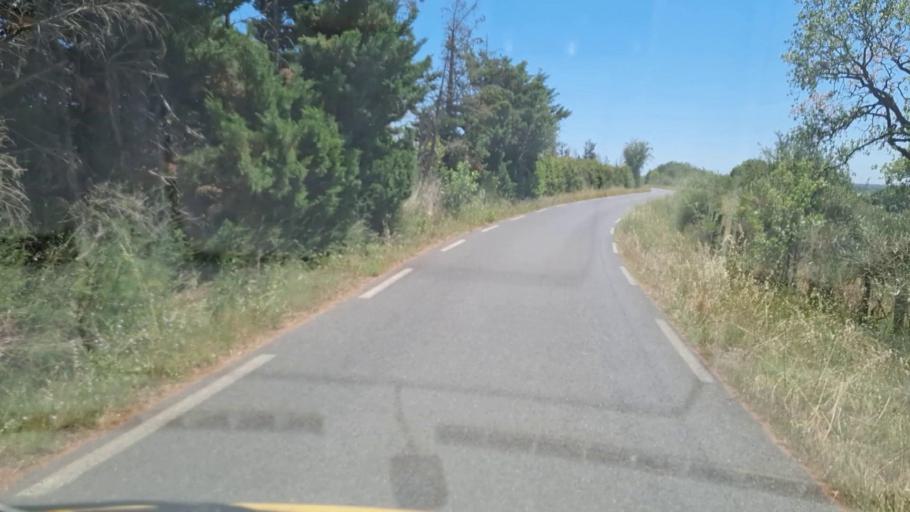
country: FR
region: Languedoc-Roussillon
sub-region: Departement du Gard
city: Le Cailar
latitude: 43.6329
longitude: 4.2523
